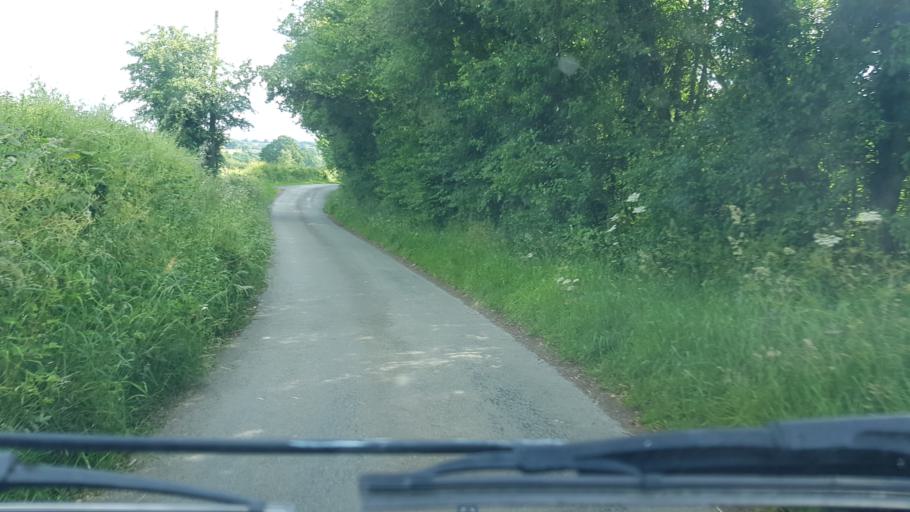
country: GB
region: England
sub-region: Shropshire
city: Romsley
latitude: 52.4455
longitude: -2.3000
